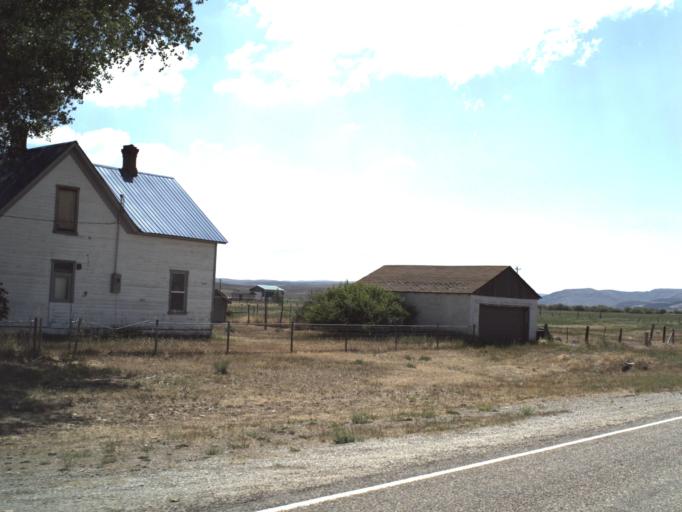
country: US
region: Utah
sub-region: Rich County
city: Randolph
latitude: 41.5241
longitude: -111.1645
